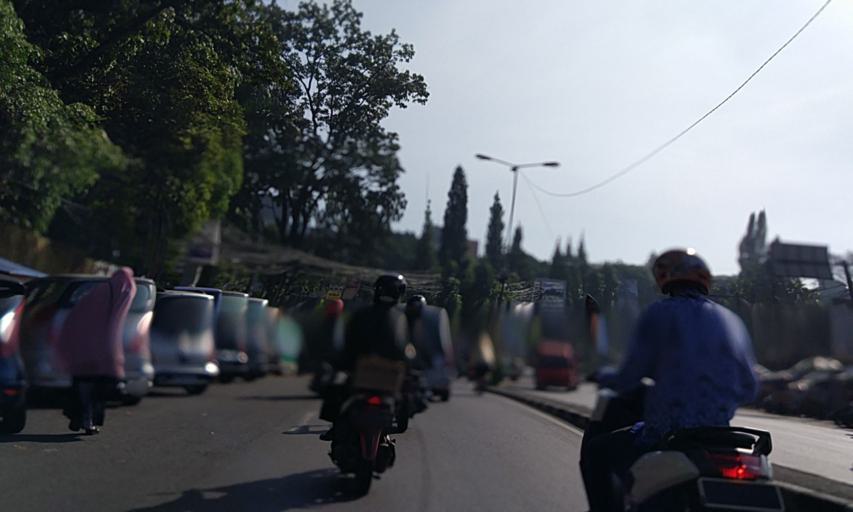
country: ID
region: West Java
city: Bandung
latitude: -6.8842
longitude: 107.6140
